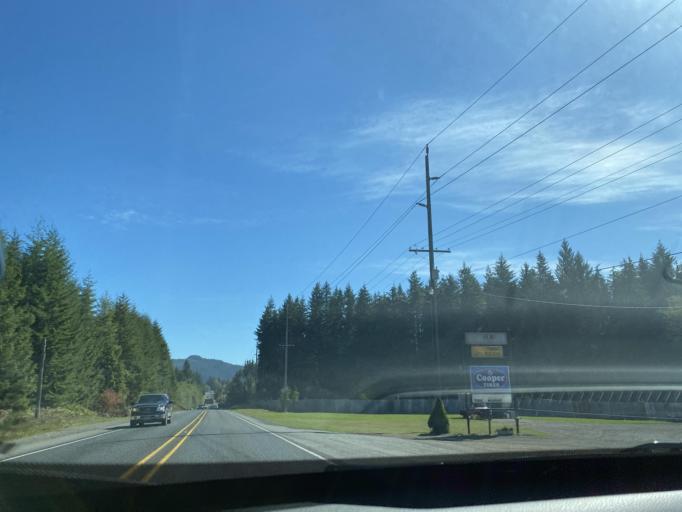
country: US
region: Washington
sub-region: Clallam County
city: Forks
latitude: 47.9628
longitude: -124.3989
